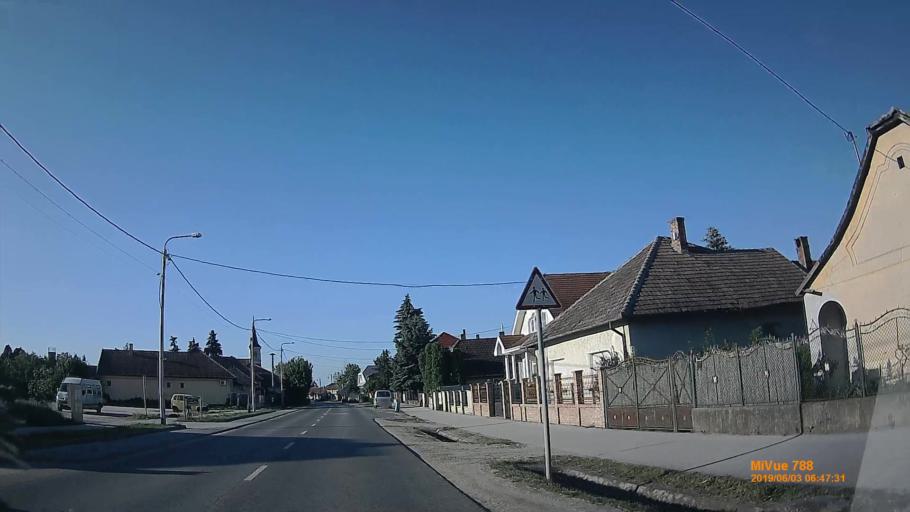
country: HU
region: Pest
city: Bugyi
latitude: 47.2254
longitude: 19.1491
